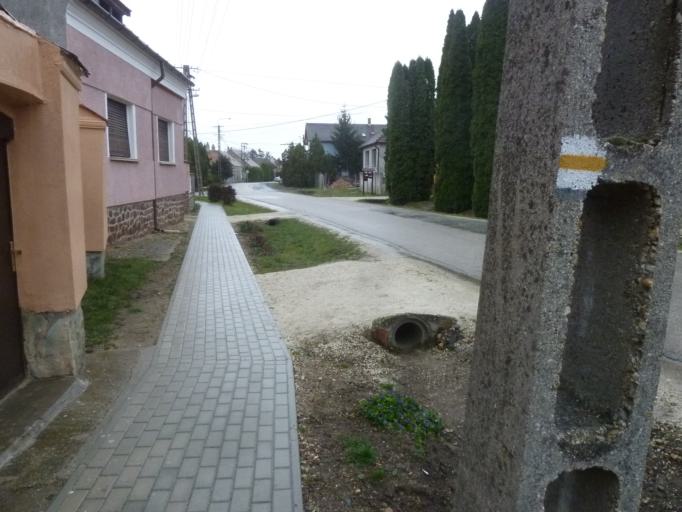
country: AT
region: Burgenland
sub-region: Politischer Bezirk Oberpullendorf
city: Lutzmannsburg
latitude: 47.4414
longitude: 16.6724
